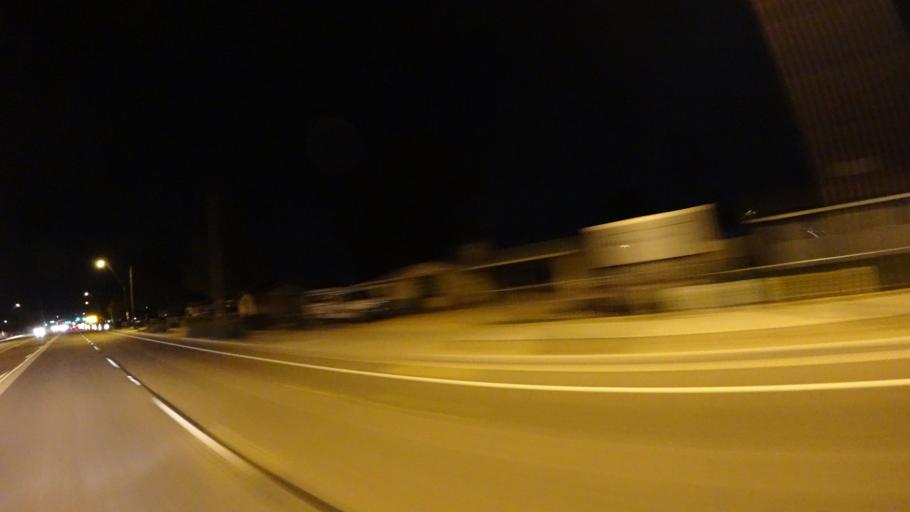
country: US
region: Arizona
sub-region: Maricopa County
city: Queen Creek
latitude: 33.2487
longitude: -111.6422
